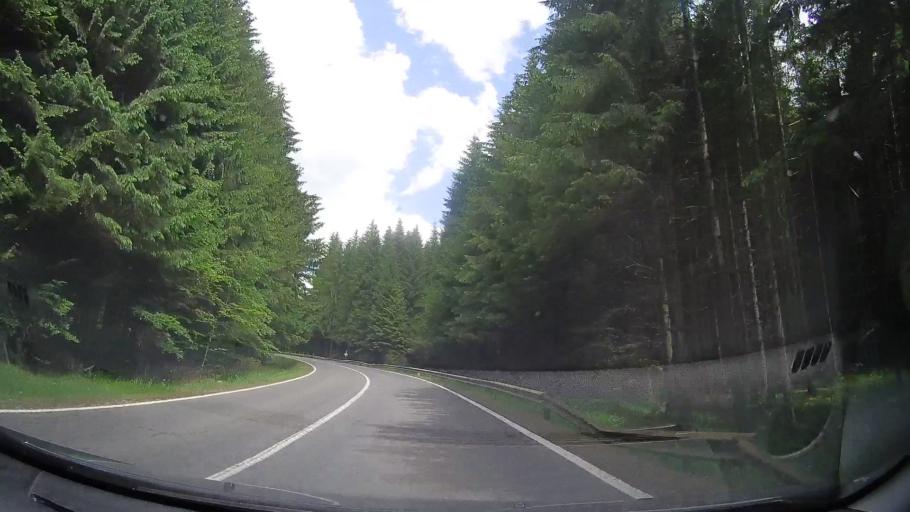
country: RO
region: Brasov
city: Crivina
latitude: 45.4600
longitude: 25.9535
